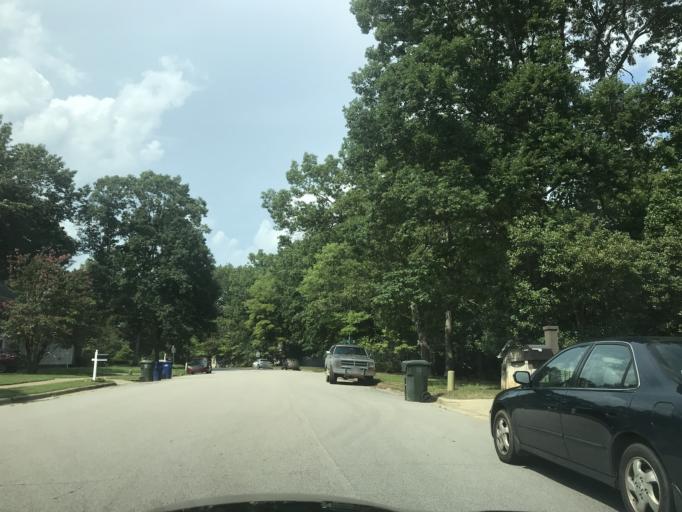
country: US
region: North Carolina
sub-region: Wake County
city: West Raleigh
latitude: 35.8776
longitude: -78.6565
